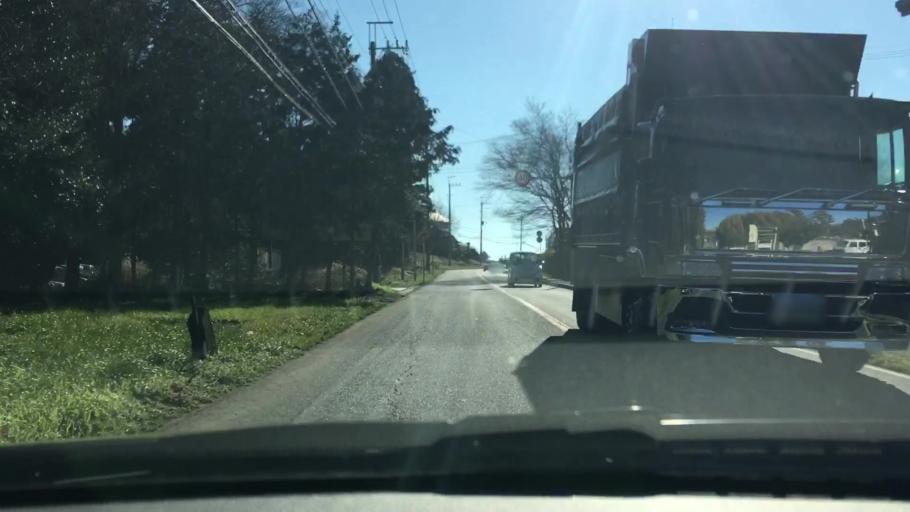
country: JP
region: Chiba
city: Shisui
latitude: 35.7103
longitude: 140.3164
